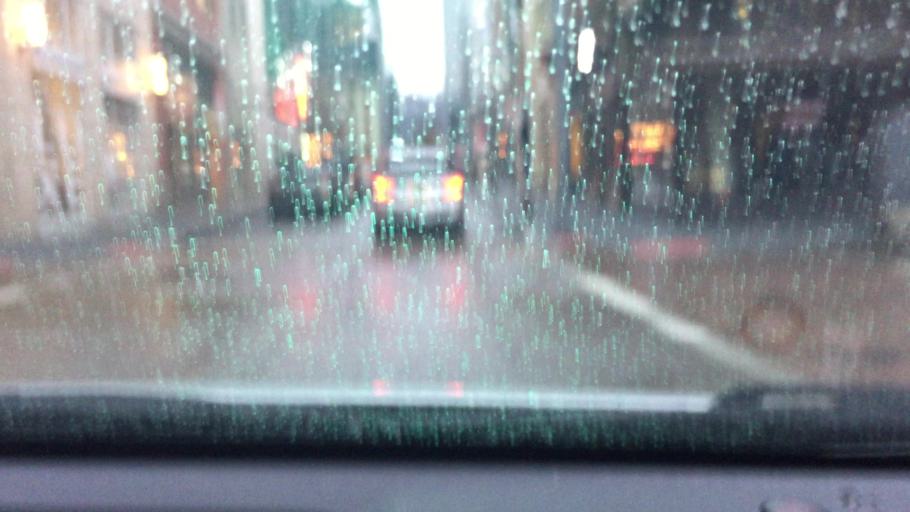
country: US
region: Pennsylvania
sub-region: Allegheny County
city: Pittsburgh
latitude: 40.4414
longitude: -80.0019
